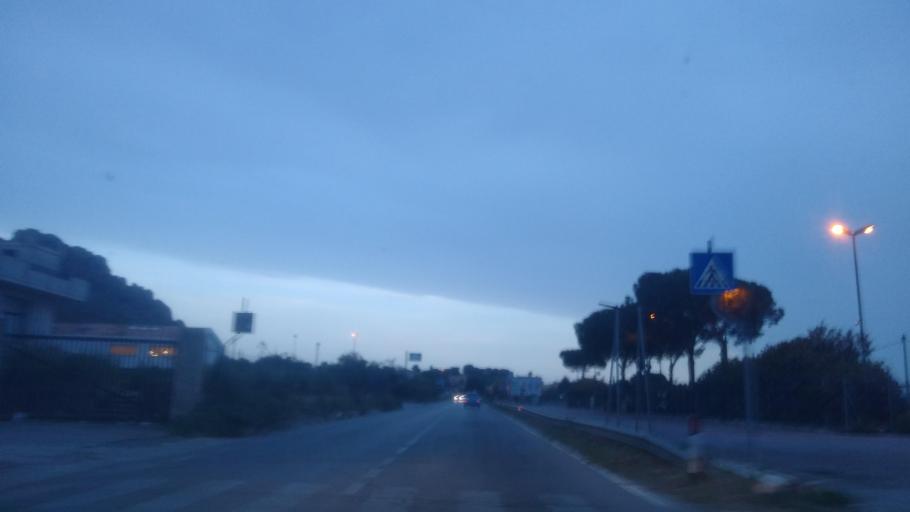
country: IT
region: Sicily
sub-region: Palermo
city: Terrasini
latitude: 38.1412
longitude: 13.0831
